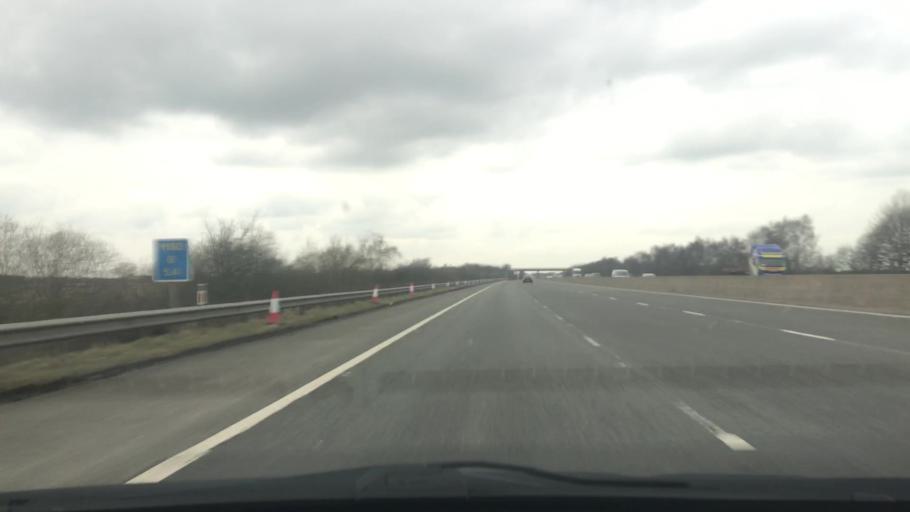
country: GB
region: England
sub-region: Doncaster
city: Hatfield
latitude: 53.5742
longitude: -0.9128
